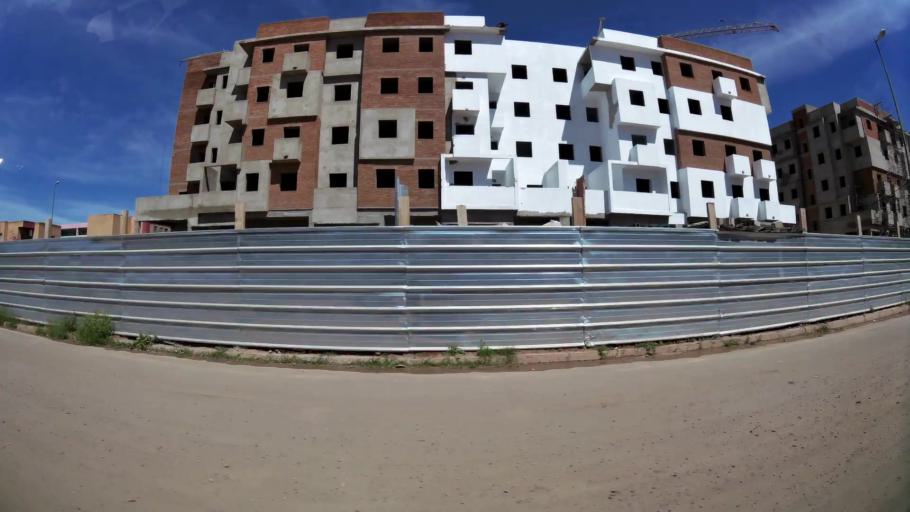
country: MA
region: Marrakech-Tensift-Al Haouz
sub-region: Marrakech
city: Marrakesh
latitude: 31.6349
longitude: -8.0744
